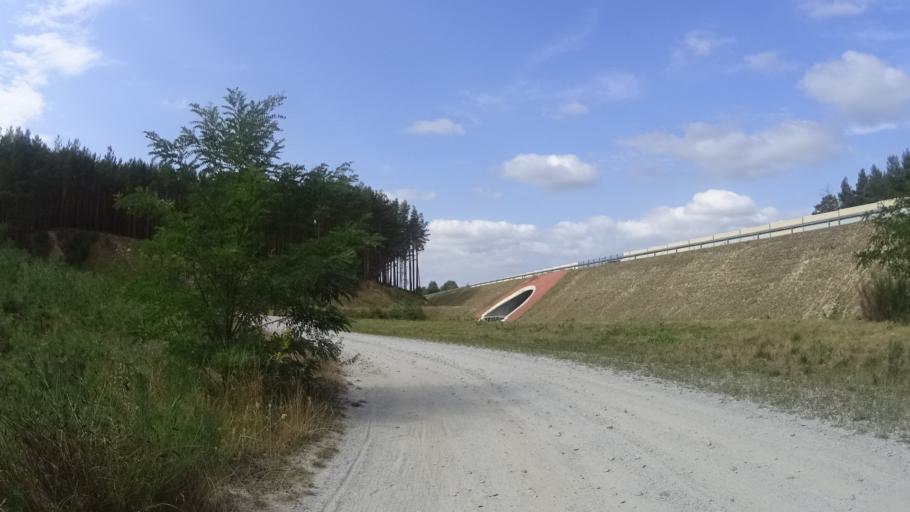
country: PL
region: Lubusz
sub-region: Powiat zarski
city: Leknica
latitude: 51.5352
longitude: 14.7511
